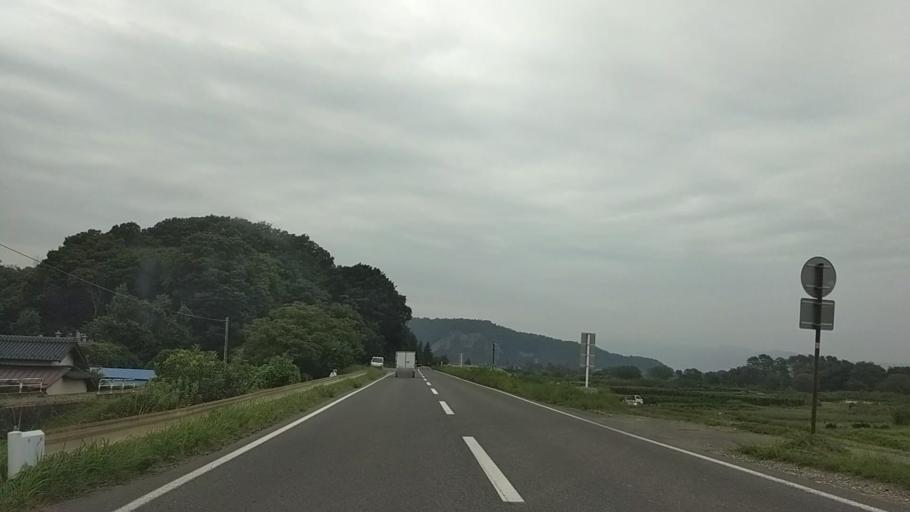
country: JP
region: Nagano
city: Nagano-shi
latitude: 36.6003
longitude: 138.2208
